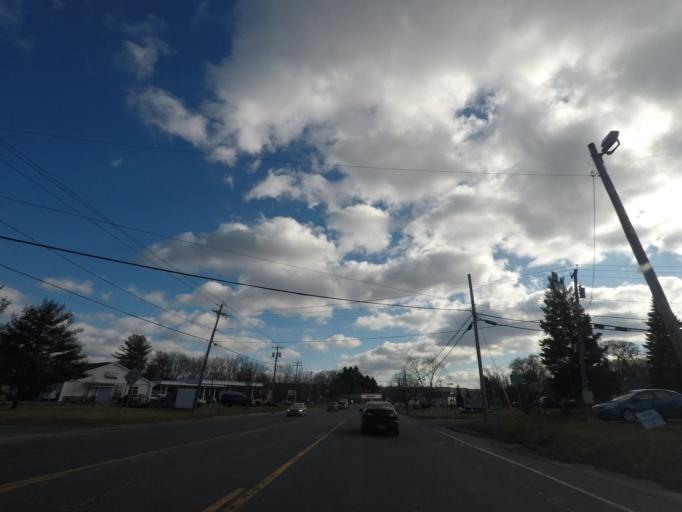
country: US
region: New York
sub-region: Schenectady County
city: Schenectady
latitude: 42.8365
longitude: -73.9340
